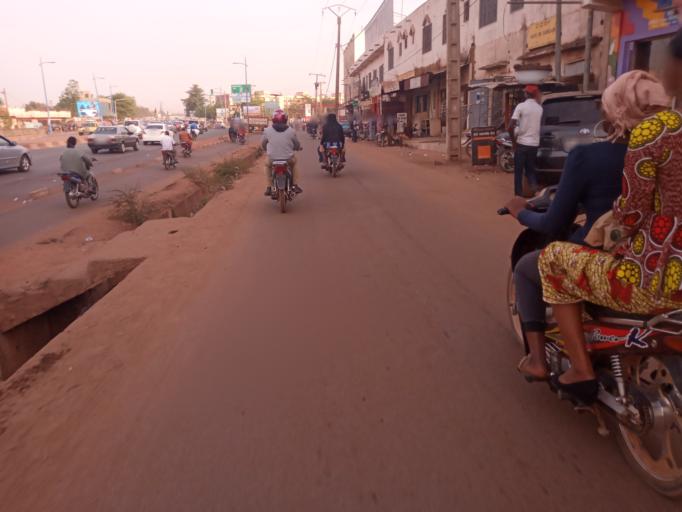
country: ML
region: Bamako
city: Bamako
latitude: 12.6072
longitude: -7.9738
